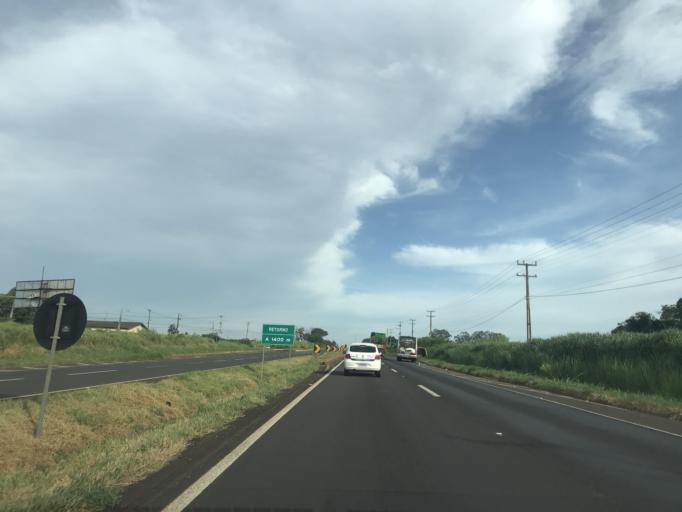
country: BR
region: Parana
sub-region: Maringa
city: Maringa
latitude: -23.4045
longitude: -51.9947
